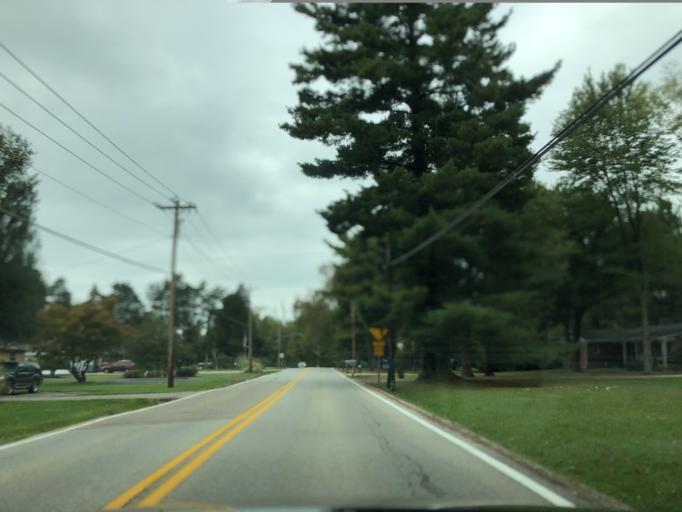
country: US
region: Ohio
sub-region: Hamilton County
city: The Village of Indian Hill
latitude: 39.2680
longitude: -84.3049
